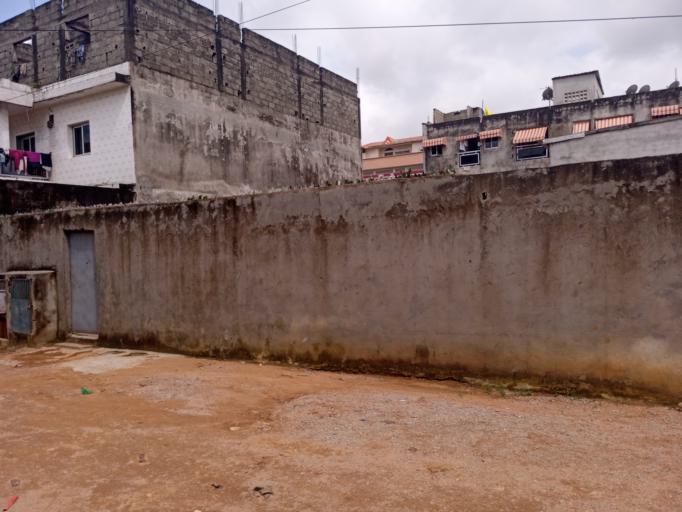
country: CI
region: Lagunes
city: Bingerville
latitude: 5.3640
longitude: -3.9574
